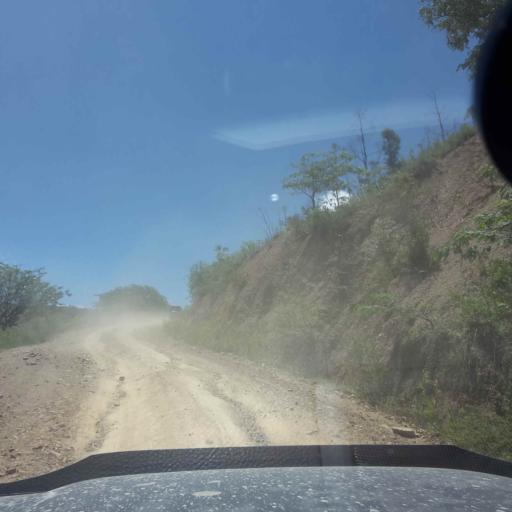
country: BO
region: Cochabamba
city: Totora
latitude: -17.7663
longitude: -65.2365
